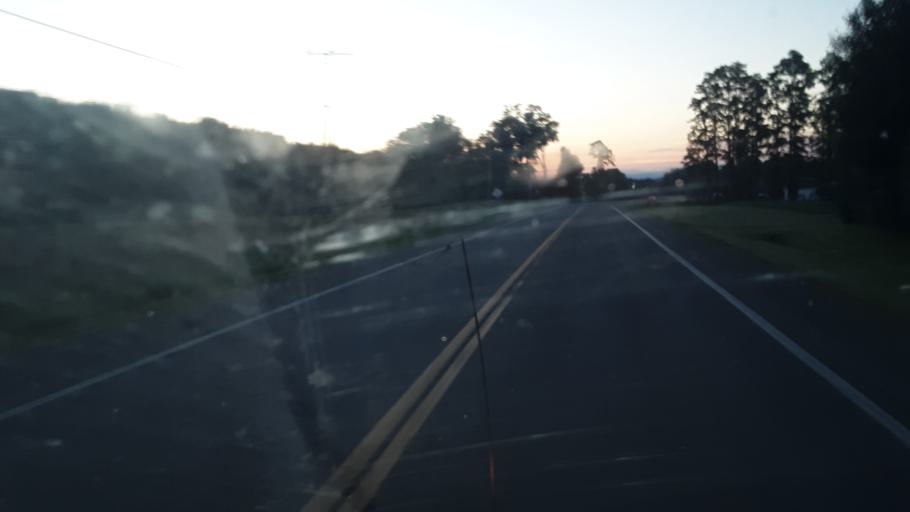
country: US
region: New York
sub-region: Montgomery County
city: Hagaman
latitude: 42.9743
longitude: -74.0382
